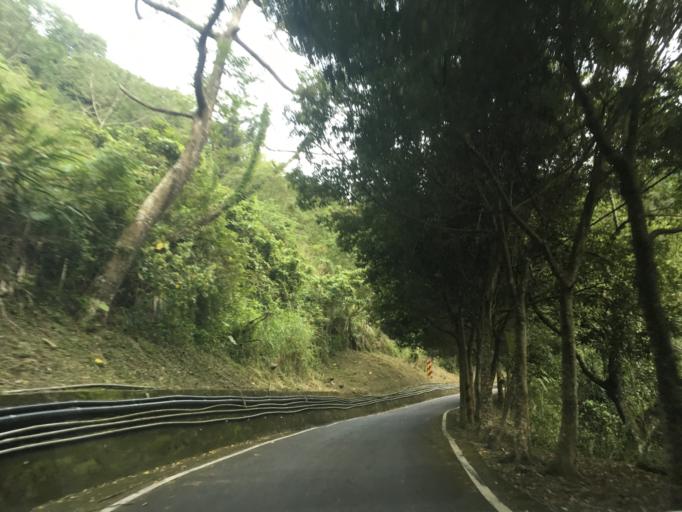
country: TW
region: Taiwan
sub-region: Nantou
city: Puli
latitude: 23.9477
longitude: 120.8551
